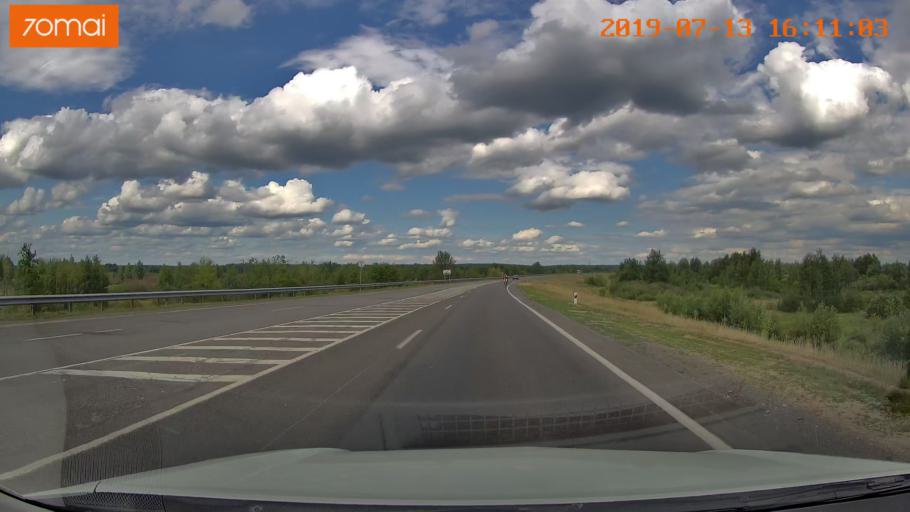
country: BY
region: Mogilev
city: Babruysk
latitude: 53.1647
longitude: 29.2484
